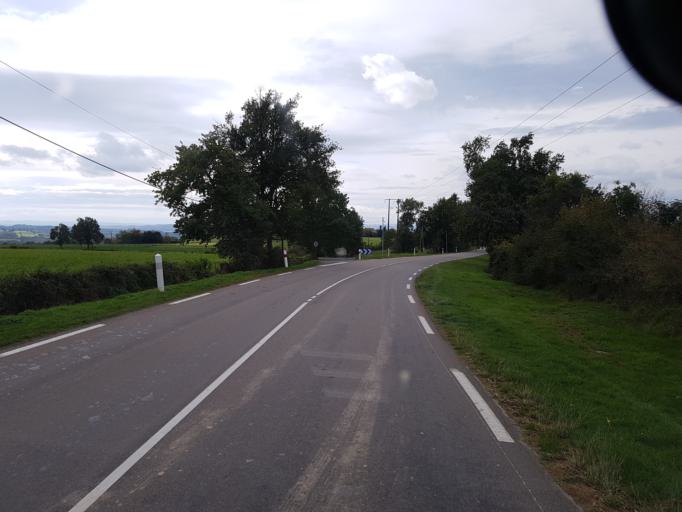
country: FR
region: Rhone-Alpes
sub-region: Departement de la Loire
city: Chazelles-sur-Lyon
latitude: 45.6242
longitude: 4.3488
